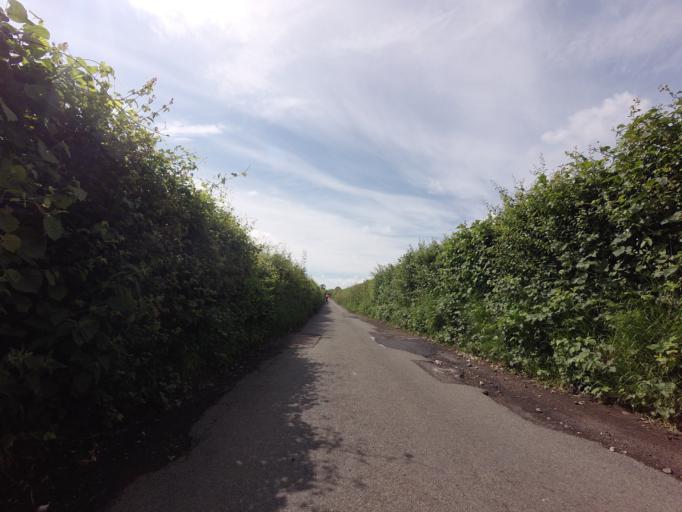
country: GB
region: England
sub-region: Greater London
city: Orpington
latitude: 51.3654
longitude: 0.1304
